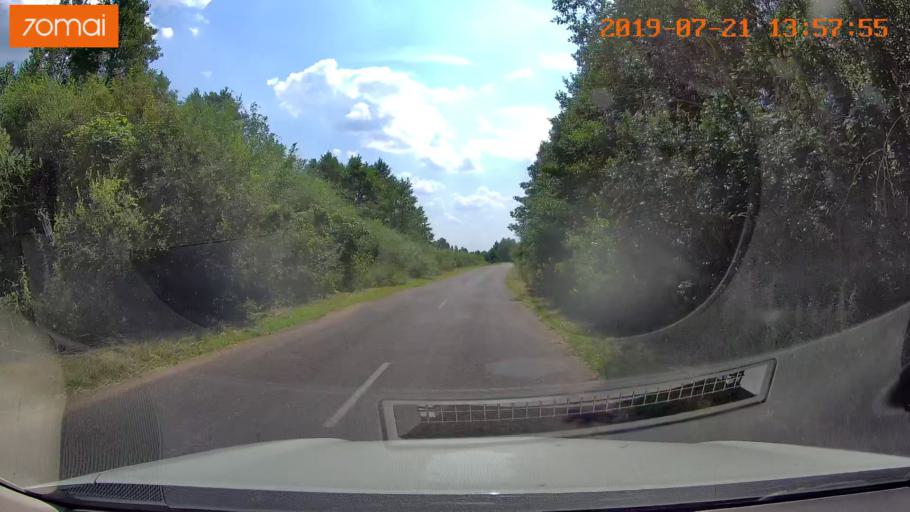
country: BY
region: Grodnenskaya
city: Lyubcha
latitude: 53.7665
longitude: 26.0866
